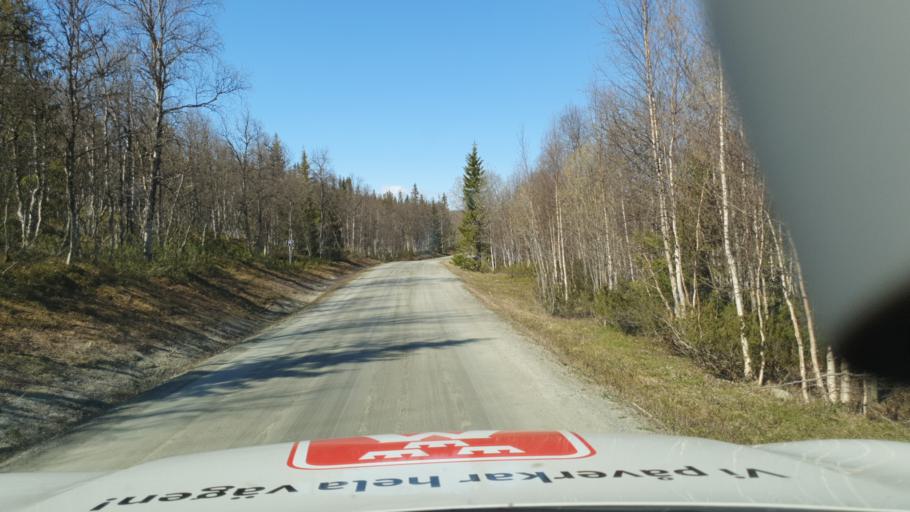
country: NO
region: Nordland
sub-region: Rana
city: Mo i Rana
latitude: 65.7068
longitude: 15.2669
